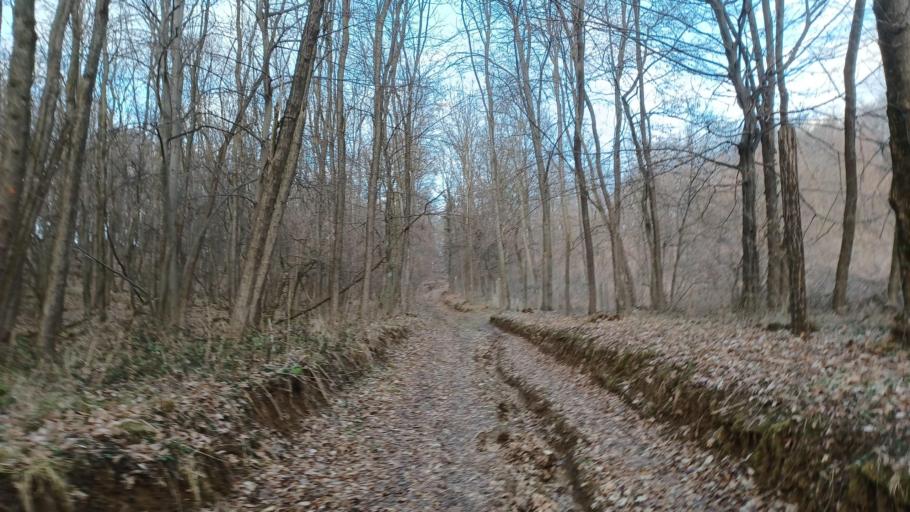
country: HU
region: Tolna
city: Szentgalpuszta
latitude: 46.3079
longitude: 18.6176
